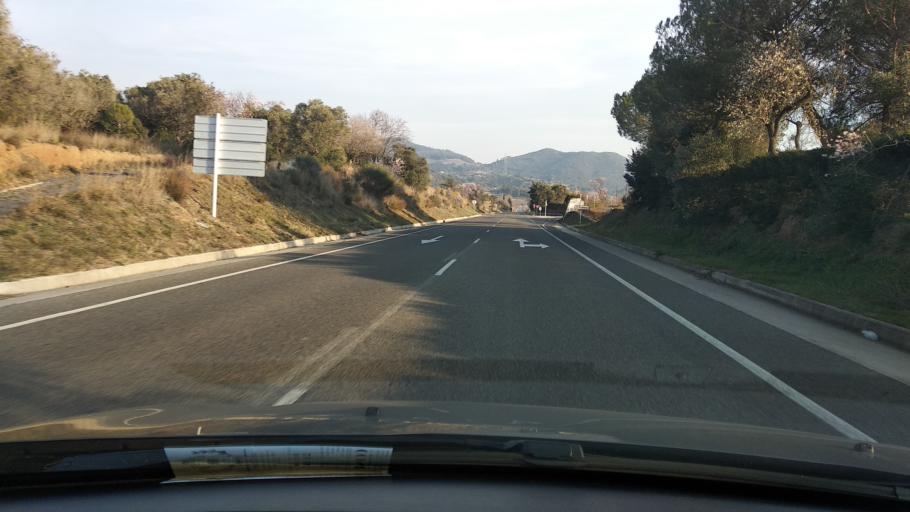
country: ES
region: Catalonia
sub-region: Provincia de Tarragona
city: Alforja
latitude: 41.2092
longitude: 0.9839
